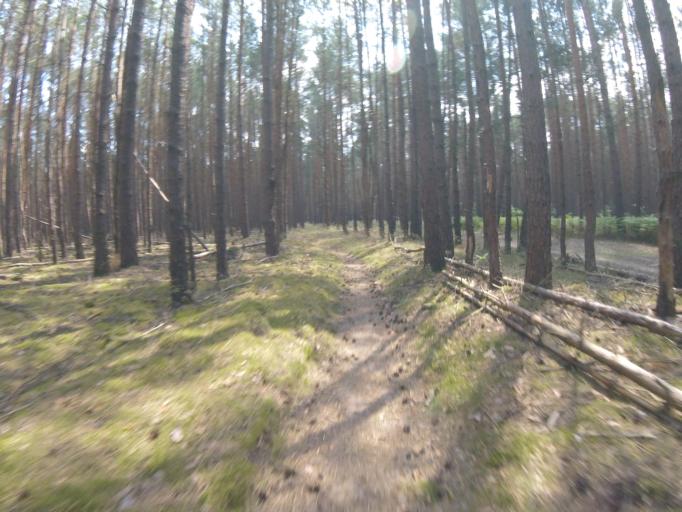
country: DE
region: Brandenburg
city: Bestensee
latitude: 52.2699
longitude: 13.6950
